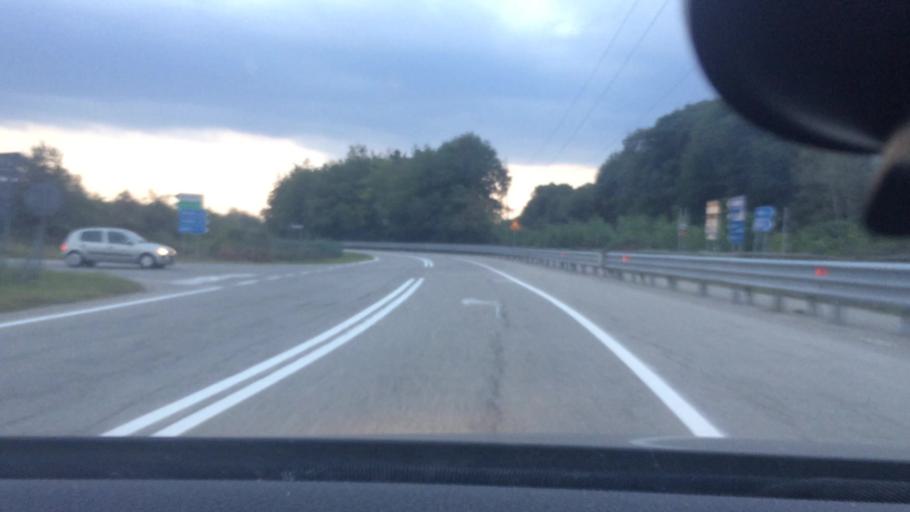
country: IT
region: Lombardy
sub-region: Provincia di Varese
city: Vizzola Ticino
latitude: 45.6111
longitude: 8.7087
